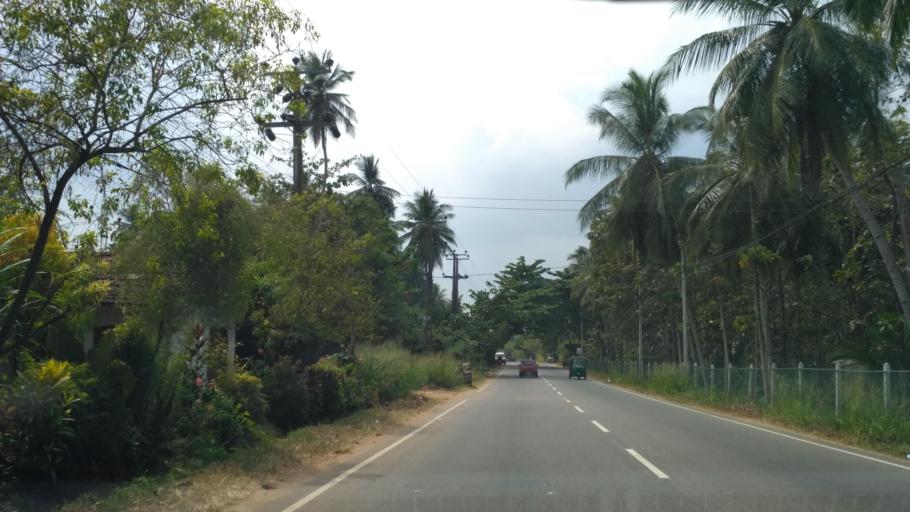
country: LK
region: North Western
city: Kuliyapitiya
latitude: 7.3269
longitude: 80.1167
